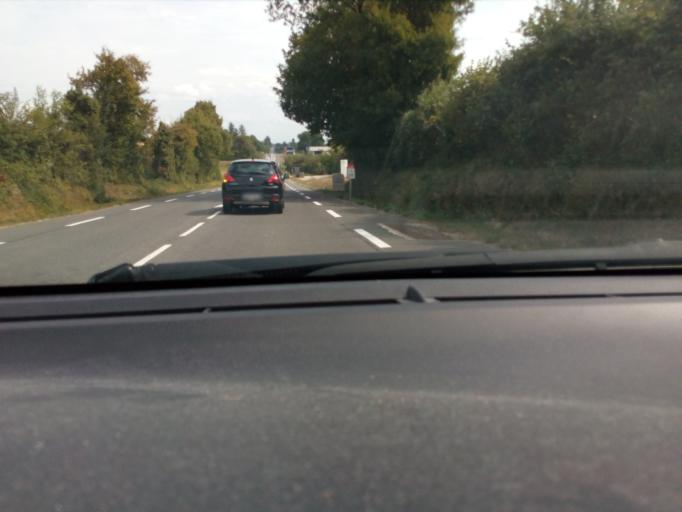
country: FR
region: Poitou-Charentes
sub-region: Departement de la Charente
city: Fleac
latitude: 45.6790
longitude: 0.0797
